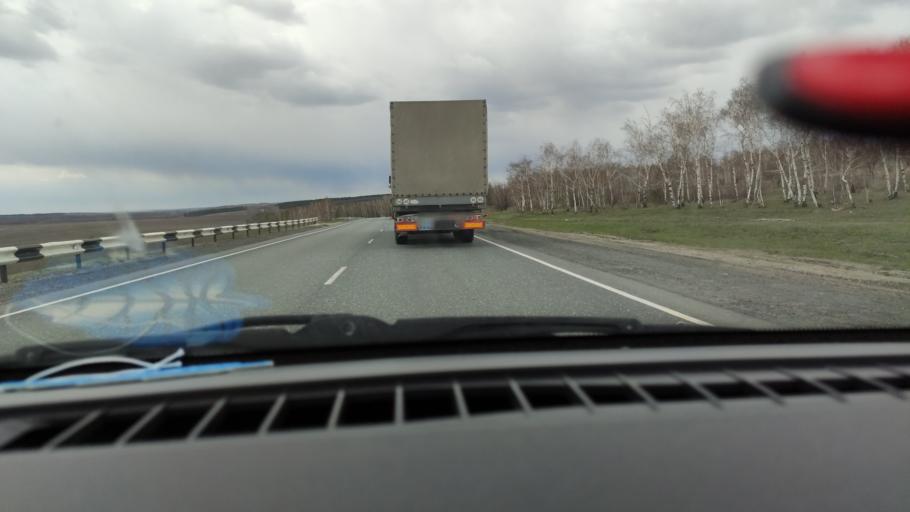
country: RU
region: Saratov
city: Sennoy
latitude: 52.1315
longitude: 46.8632
